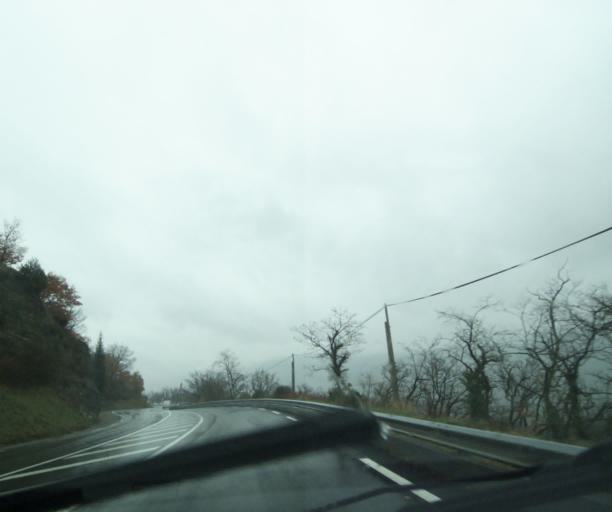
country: FR
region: Rhone-Alpes
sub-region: Departement de l'Ardeche
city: Saint-Priest
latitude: 44.7264
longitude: 4.5473
